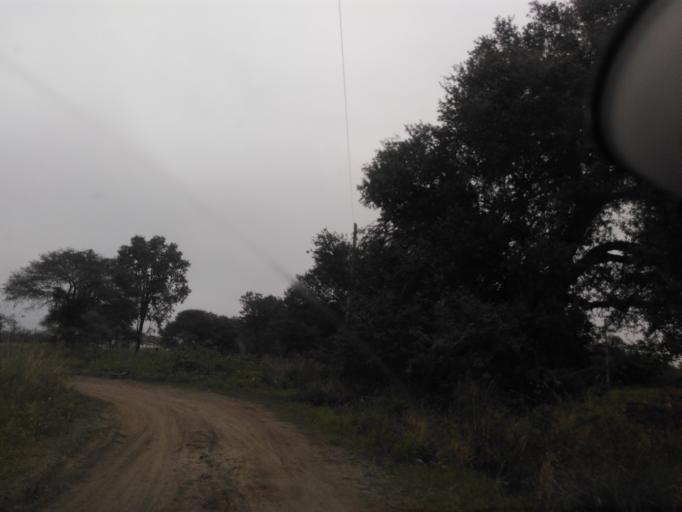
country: AR
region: Chaco
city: Fontana
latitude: -27.4000
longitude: -58.9948
